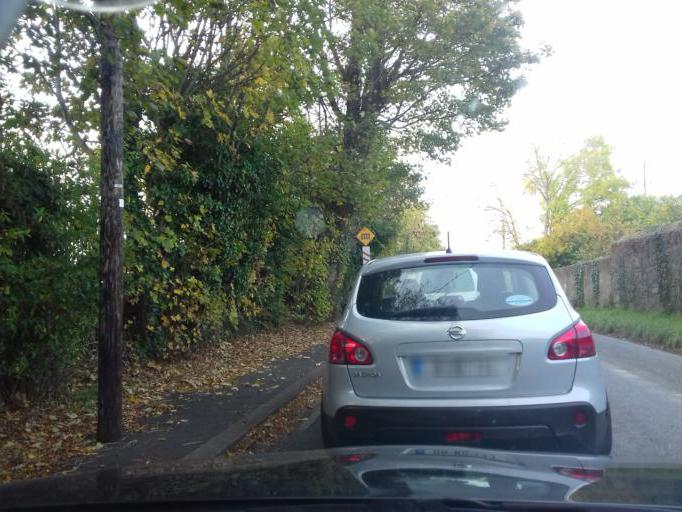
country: IE
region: Leinster
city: Hartstown
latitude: 53.3813
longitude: -6.4225
